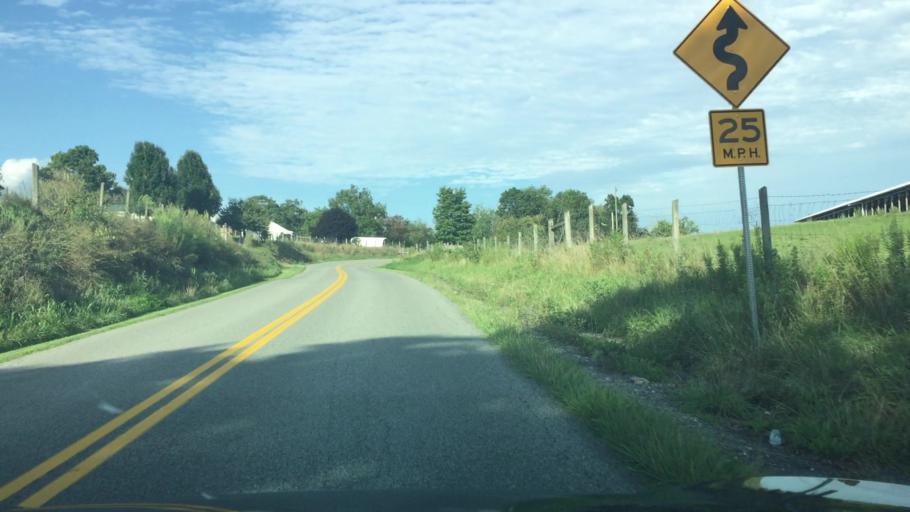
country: US
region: Virginia
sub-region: Wythe County
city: Wytheville
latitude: 36.9393
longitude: -80.9686
